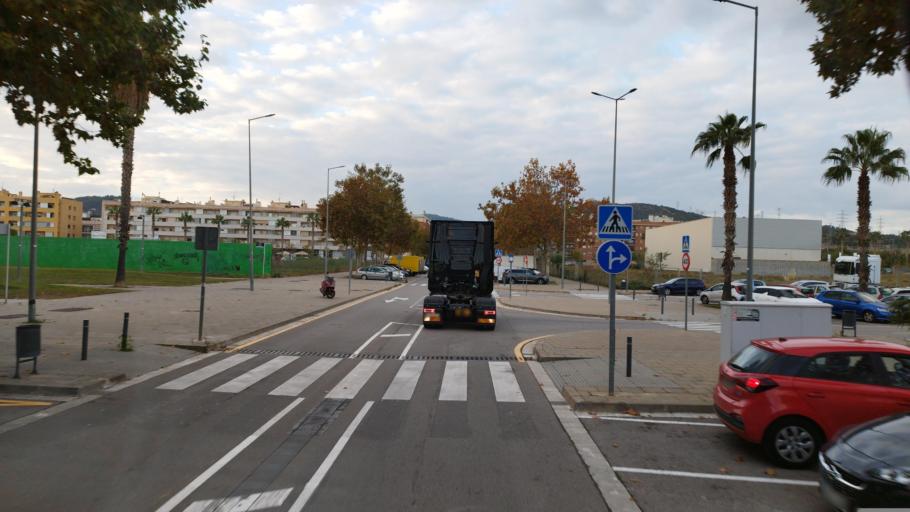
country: ES
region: Catalonia
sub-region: Provincia de Barcelona
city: Viladecans
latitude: 41.3154
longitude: 2.0313
